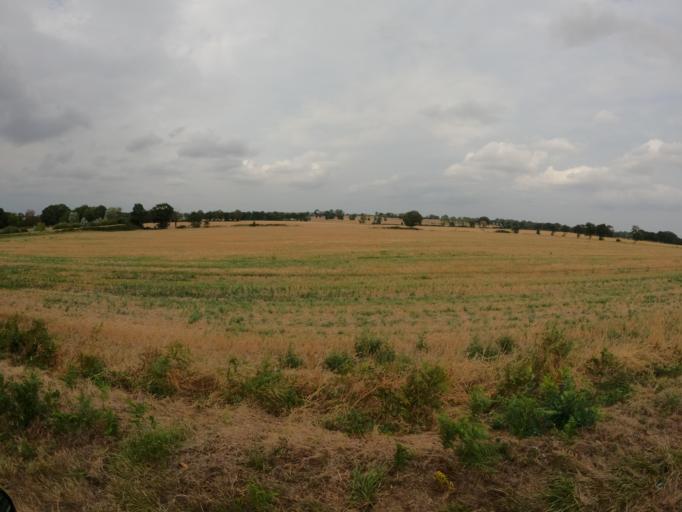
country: FR
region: Pays de la Loire
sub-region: Departement de Maine-et-Loire
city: La Romagne
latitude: 47.0519
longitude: -1.0061
